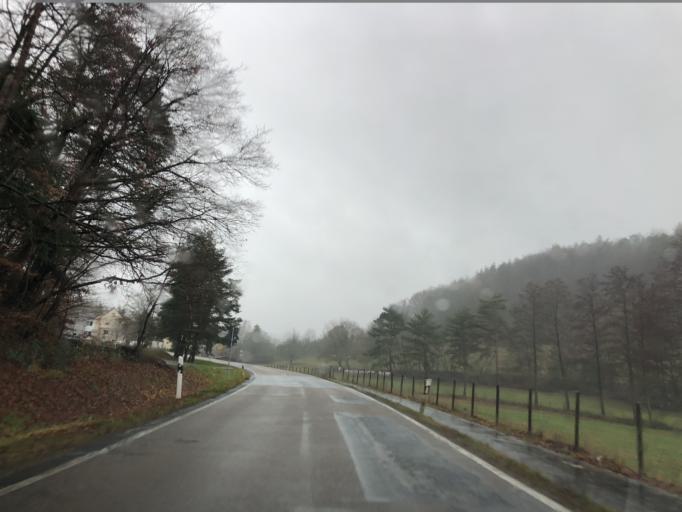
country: DE
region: Hesse
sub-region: Regierungsbezirk Darmstadt
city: Lutzelbach
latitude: 49.7716
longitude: 9.1063
